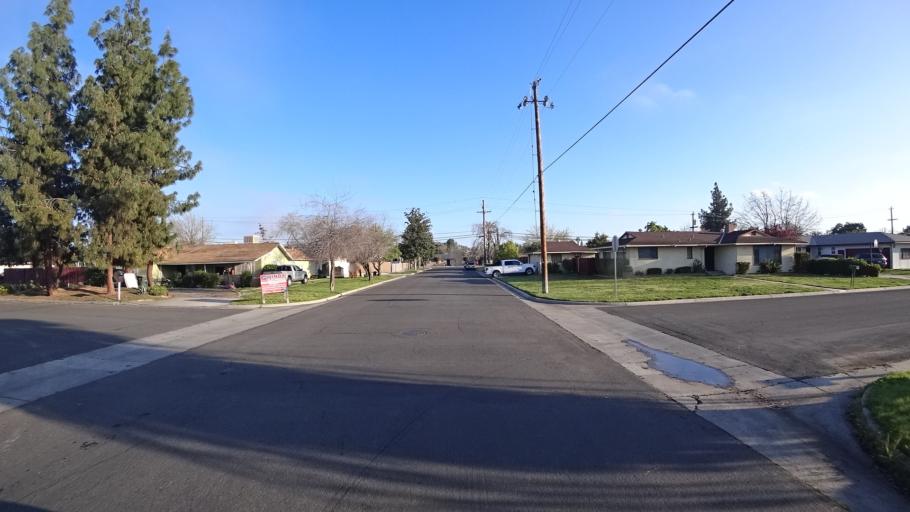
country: US
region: California
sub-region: Fresno County
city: Fresno
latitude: 36.8112
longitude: -119.7791
